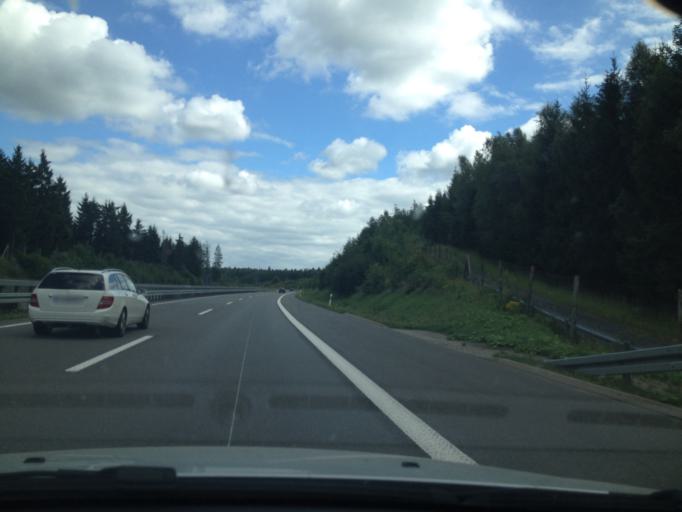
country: DE
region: North Rhine-Westphalia
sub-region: Regierungsbezirk Arnsberg
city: Wenden
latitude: 50.9938
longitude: 7.8972
